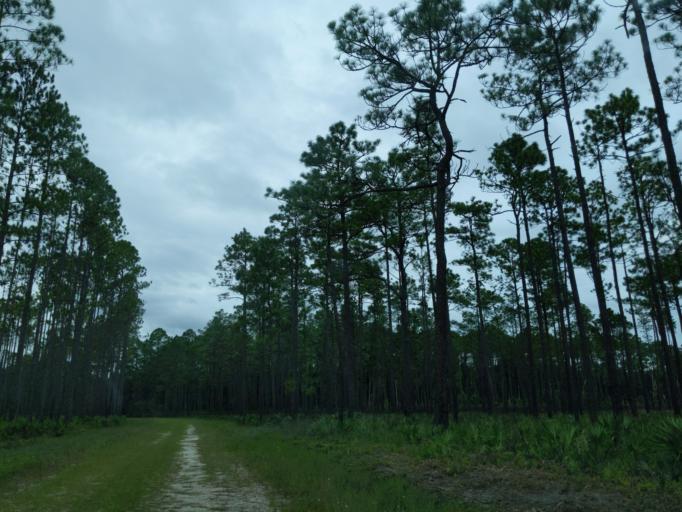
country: US
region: Florida
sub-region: Gadsden County
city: Midway
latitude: 30.3670
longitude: -84.4721
